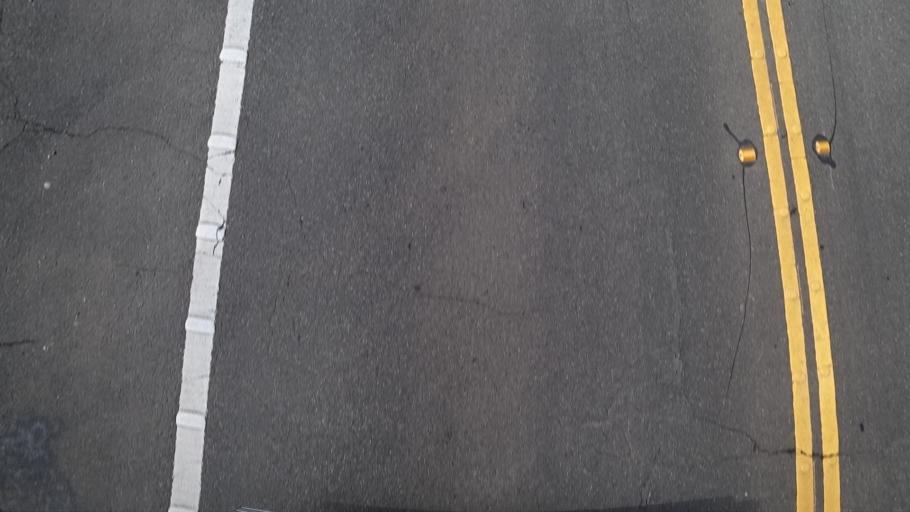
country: US
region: California
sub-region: Butte County
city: Paradise
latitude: 39.6396
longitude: -121.6655
